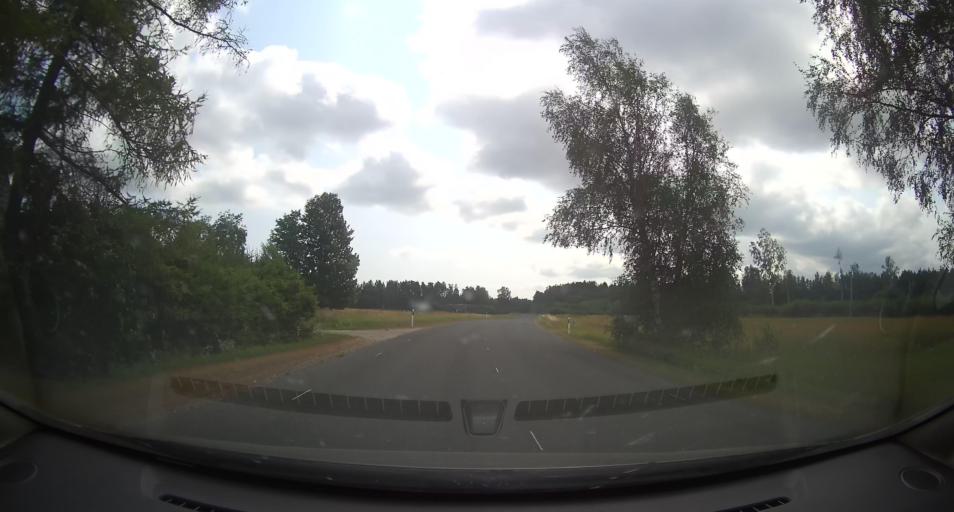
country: EE
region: Paernumaa
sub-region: Audru vald
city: Audru
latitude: 58.4362
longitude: 24.3104
